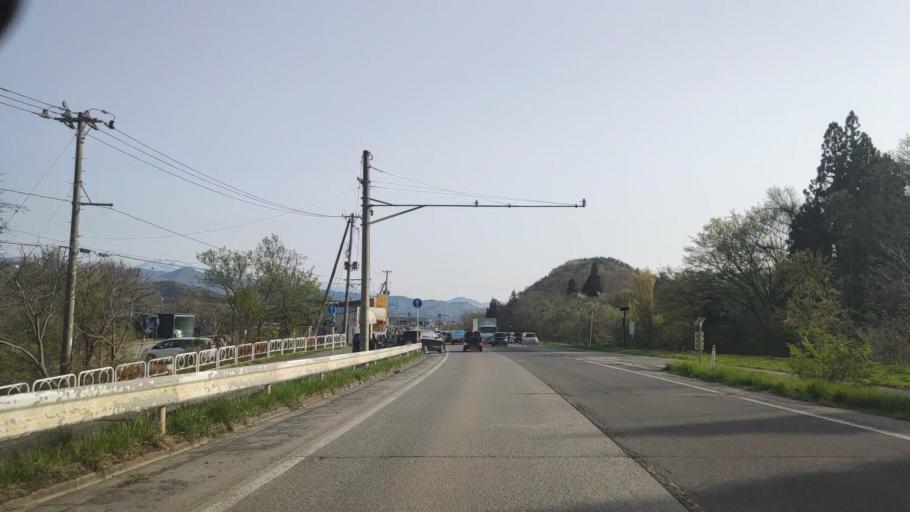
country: JP
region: Aomori
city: Aomori Shi
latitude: 40.8537
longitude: 140.8388
